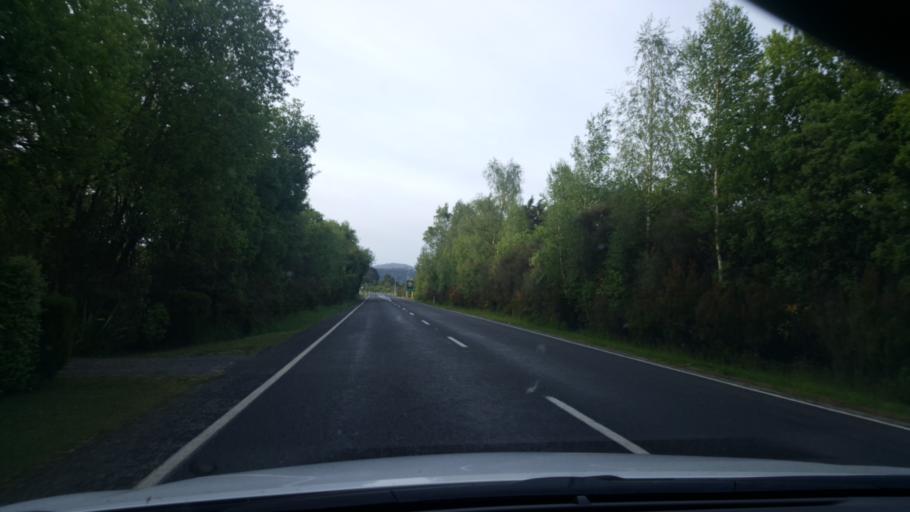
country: NZ
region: Waikato
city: Turangi
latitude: -38.9671
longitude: 175.7677
